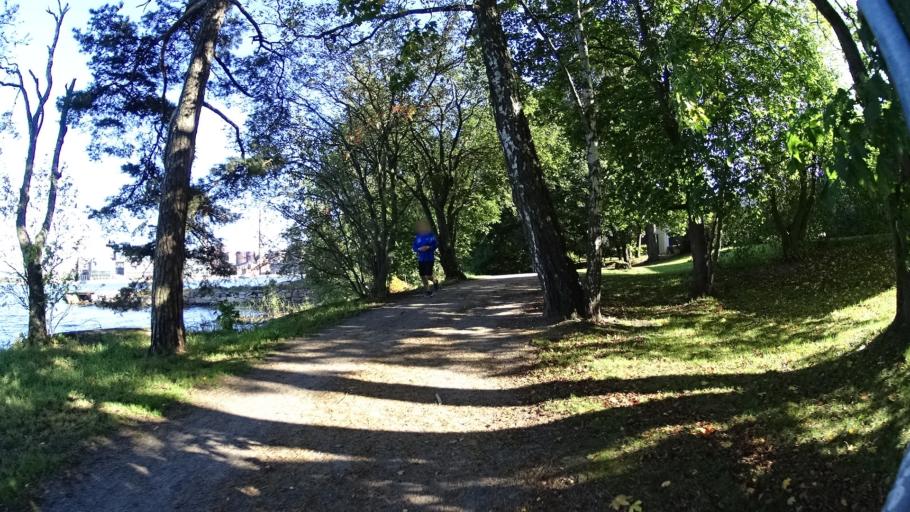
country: FI
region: Uusimaa
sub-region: Helsinki
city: Helsinki
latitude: 60.1641
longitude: 24.8902
